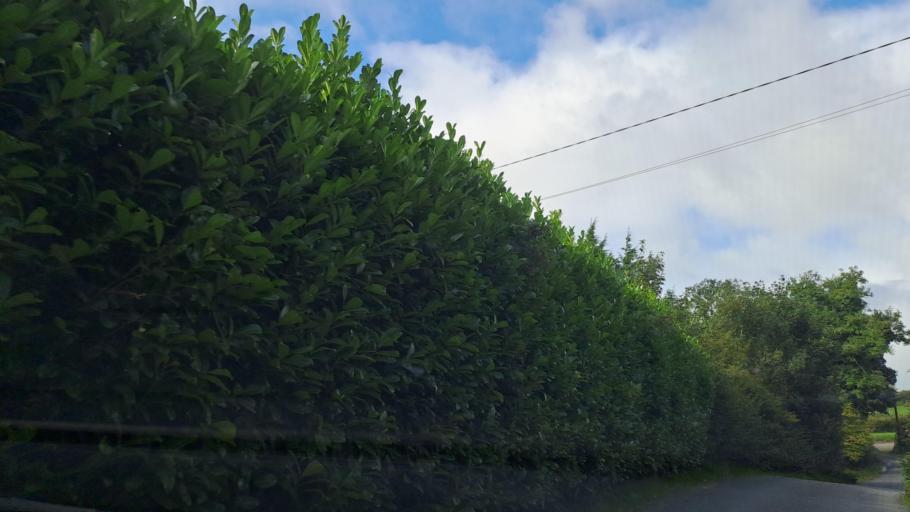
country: IE
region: Ulster
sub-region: An Cabhan
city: Kingscourt
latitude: 53.9714
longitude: -6.8824
